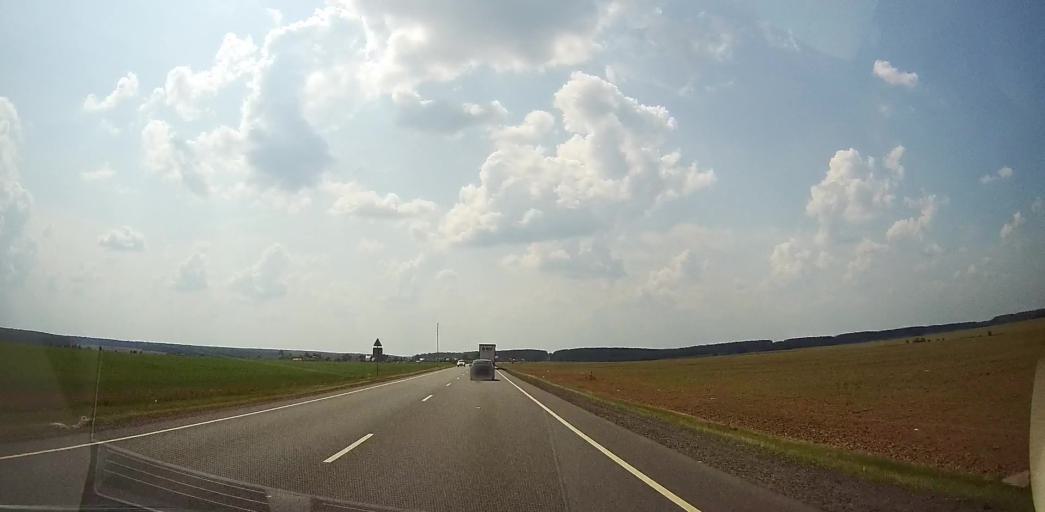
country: RU
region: Moskovskaya
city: Malino
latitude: 55.1305
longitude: 38.2509
